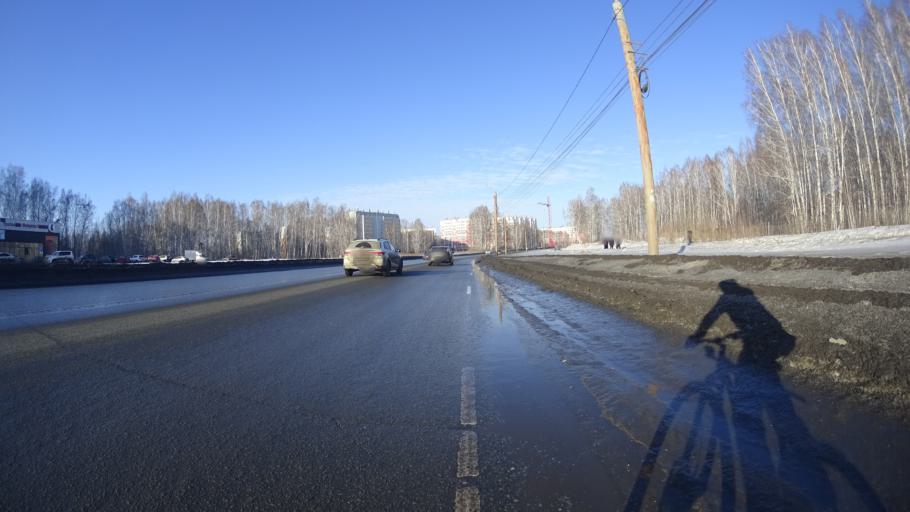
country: RU
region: Chelyabinsk
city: Roshchino
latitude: 55.2134
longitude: 61.2846
